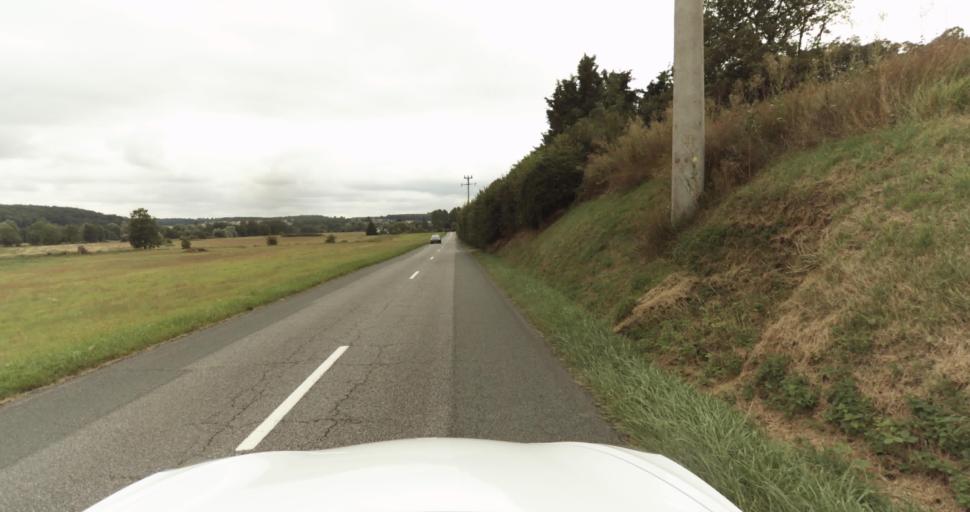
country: FR
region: Haute-Normandie
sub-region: Departement de l'Eure
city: Arnieres-sur-Iton
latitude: 49.0095
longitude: 1.1051
